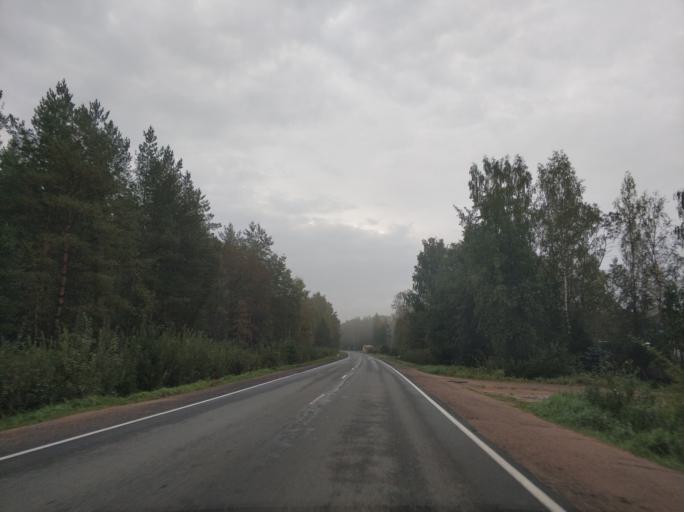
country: RU
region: Leningrad
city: Shcheglovo
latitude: 60.0941
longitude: 30.8501
